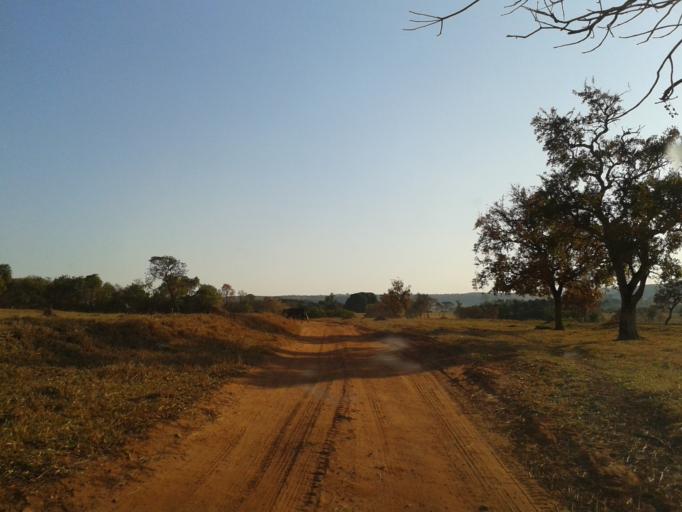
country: BR
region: Minas Gerais
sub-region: Campina Verde
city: Campina Verde
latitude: -19.2602
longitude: -49.6135
